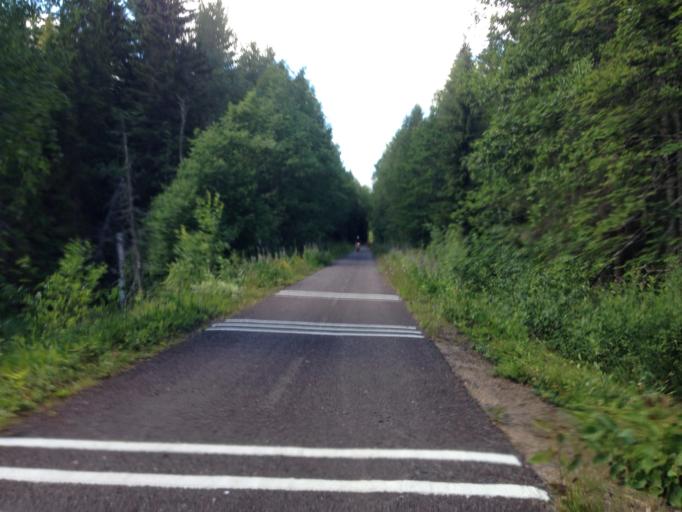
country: SE
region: Dalarna
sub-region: Ludvika Kommun
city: Grangesberg
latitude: 60.2073
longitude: 15.0557
